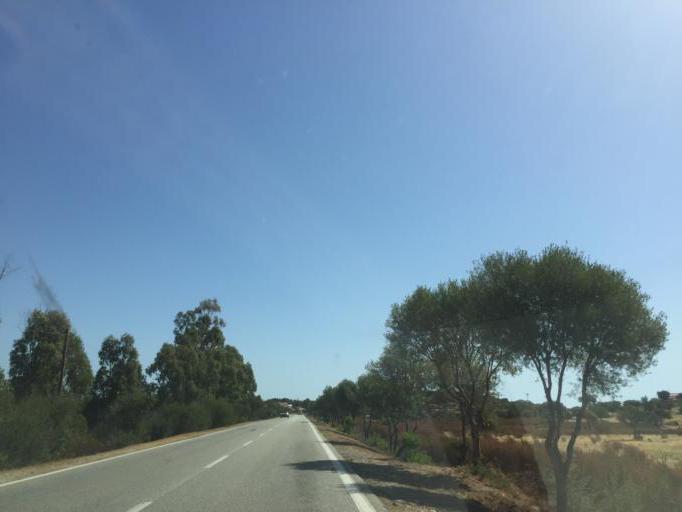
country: IT
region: Sardinia
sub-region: Provincia di Olbia-Tempio
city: San Teodoro
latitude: 40.7631
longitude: 9.6625
